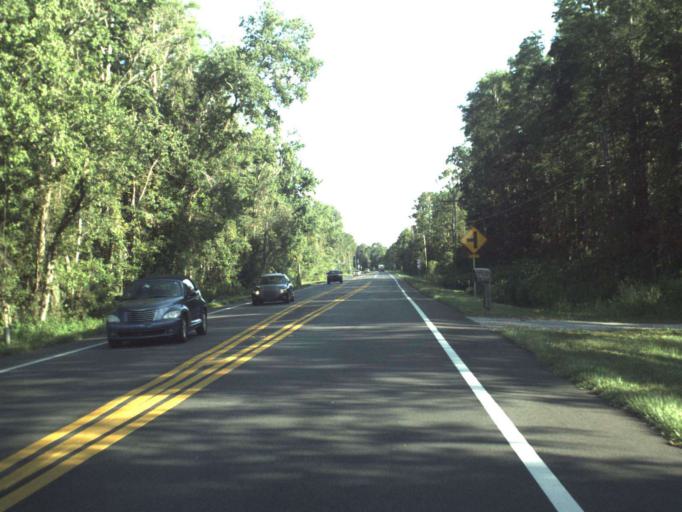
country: US
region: Florida
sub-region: Lake County
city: Clermont
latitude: 28.3790
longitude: -81.8237
